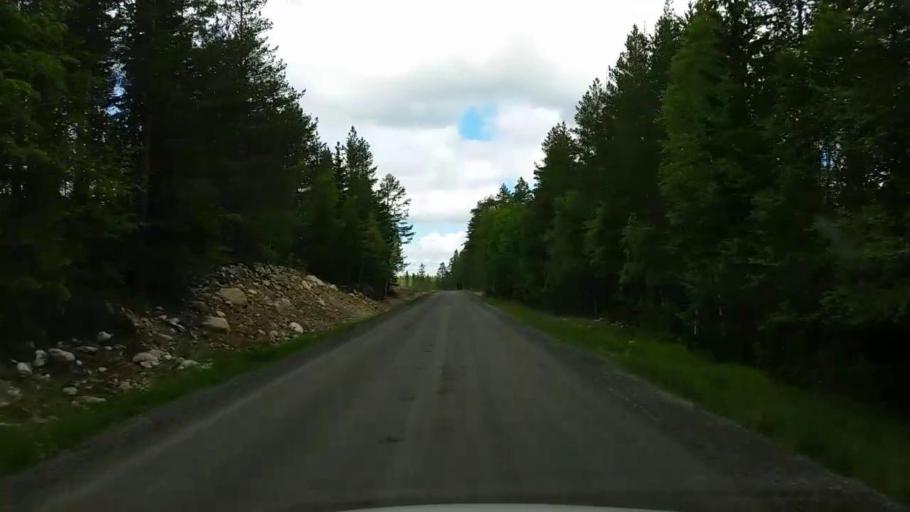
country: SE
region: Gaevleborg
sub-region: Bollnas Kommun
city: Vittsjo
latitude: 61.1642
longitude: 16.1565
